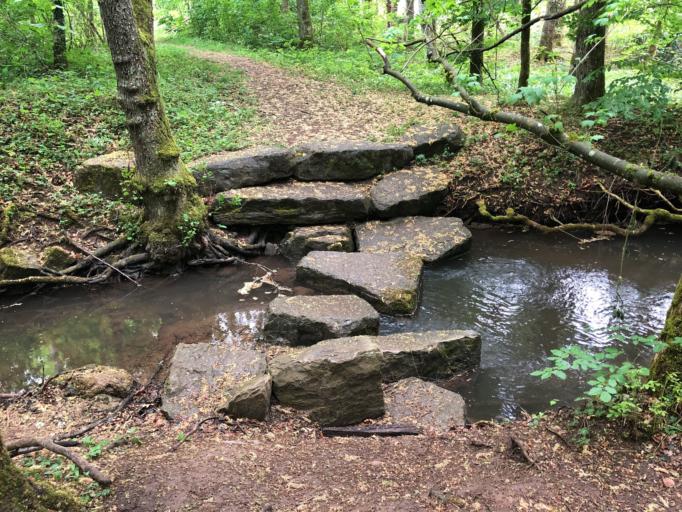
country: DE
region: Baden-Wuerttemberg
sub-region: Tuebingen Region
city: Ofterdingen
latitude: 48.4605
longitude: 9.0009
